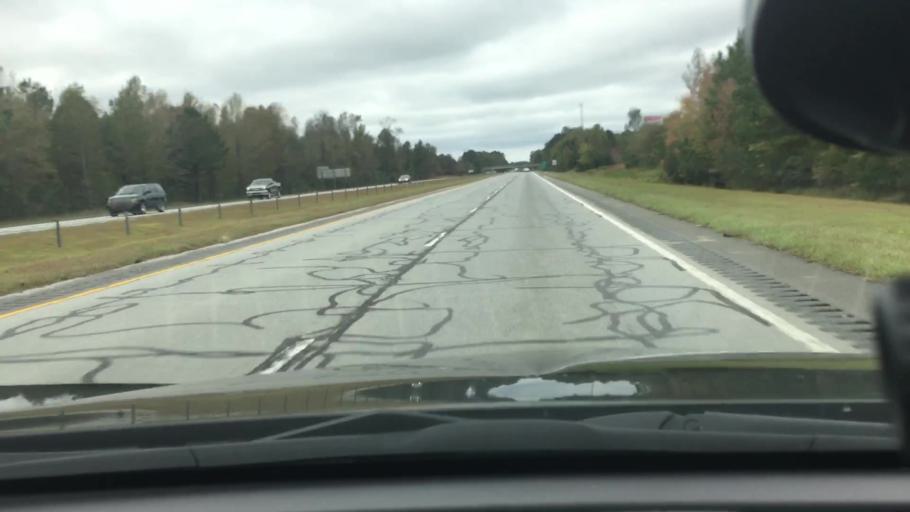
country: US
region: North Carolina
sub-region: Pitt County
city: Farmville
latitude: 35.6039
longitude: -77.5662
